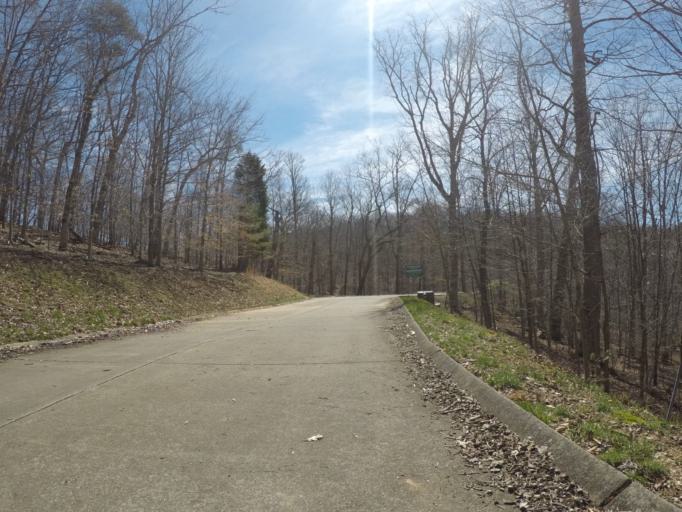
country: US
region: West Virginia
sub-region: Cabell County
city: Pea Ridge
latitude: 38.4053
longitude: -82.3397
